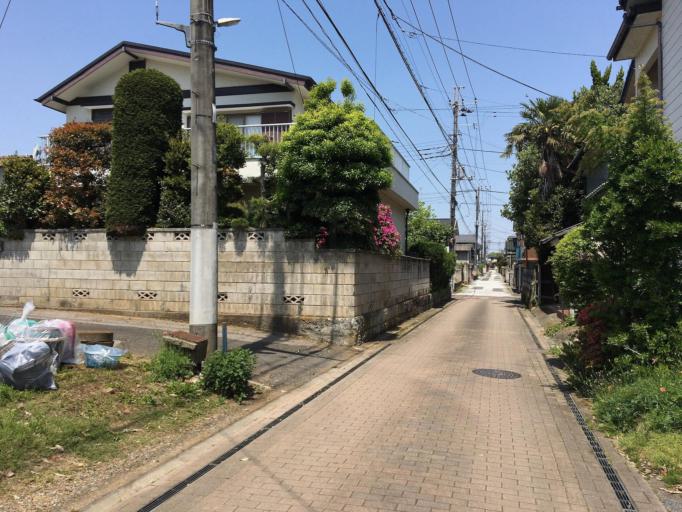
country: JP
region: Ibaraki
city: Koga
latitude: 36.1976
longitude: 139.6984
